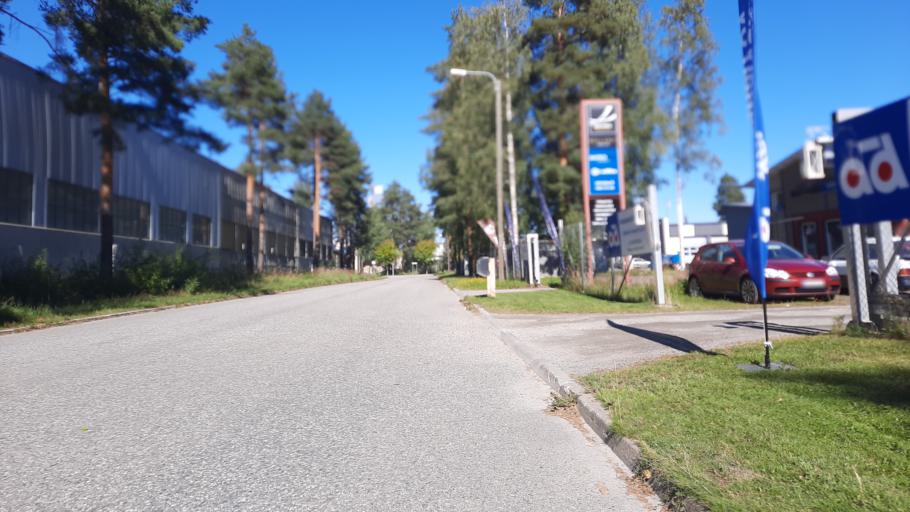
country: FI
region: North Karelia
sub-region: Joensuu
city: Joensuu
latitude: 62.6201
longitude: 29.7561
